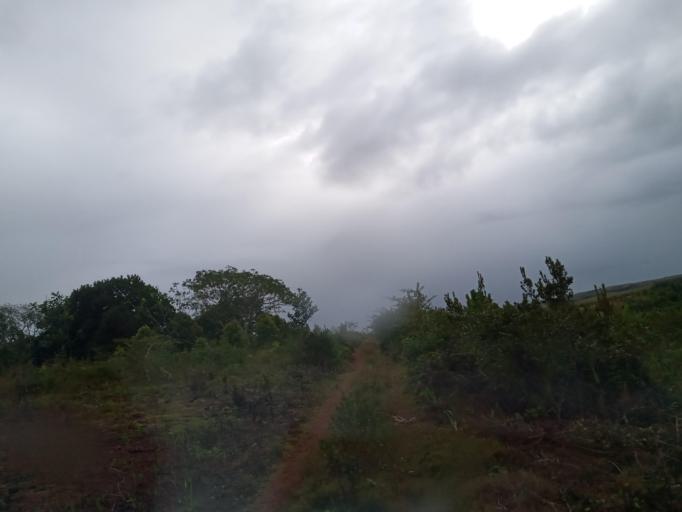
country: MG
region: Atsimo-Atsinanana
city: Vohipaho
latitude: -24.0013
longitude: 47.4041
